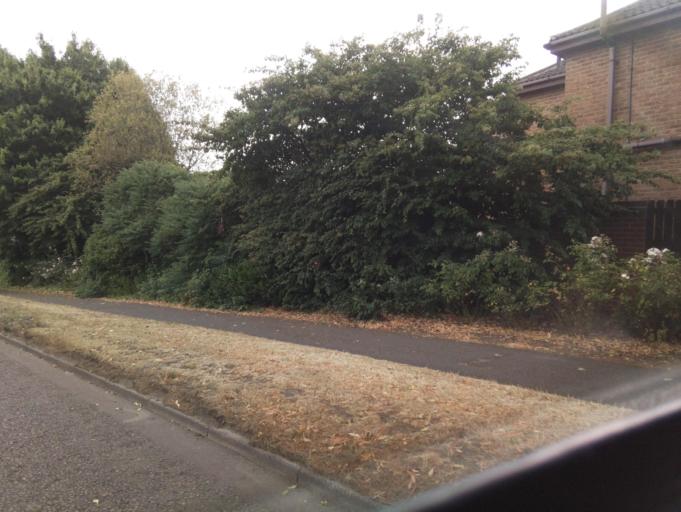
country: GB
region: England
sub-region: Derbyshire
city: Long Eaton
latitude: 52.8977
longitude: -1.2935
